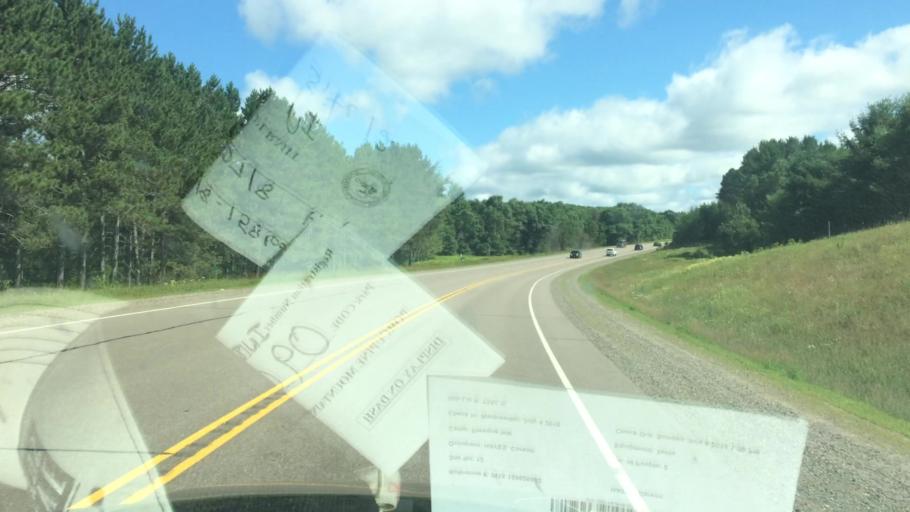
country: US
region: Wisconsin
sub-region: Oneida County
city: Rhinelander
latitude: 45.5908
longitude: -89.5691
